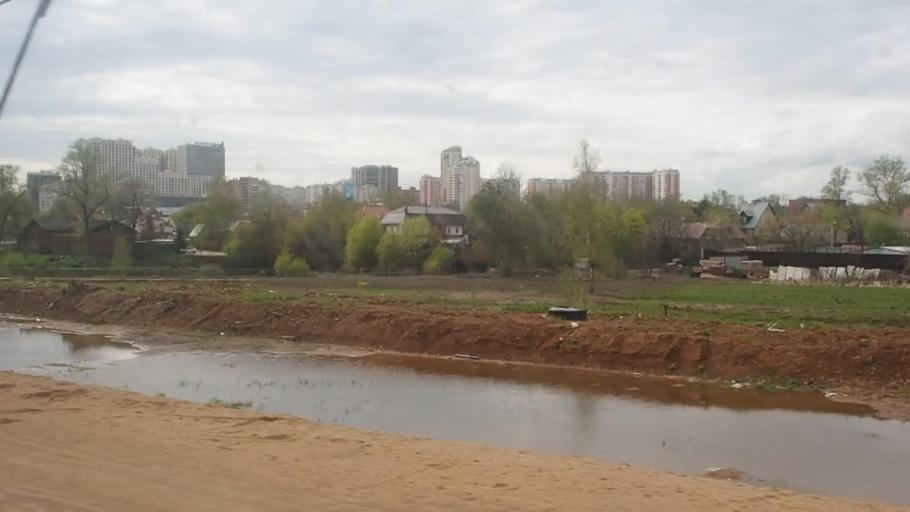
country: RU
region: Moscow
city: Novo-Peredelkino
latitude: 55.6865
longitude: 37.3250
